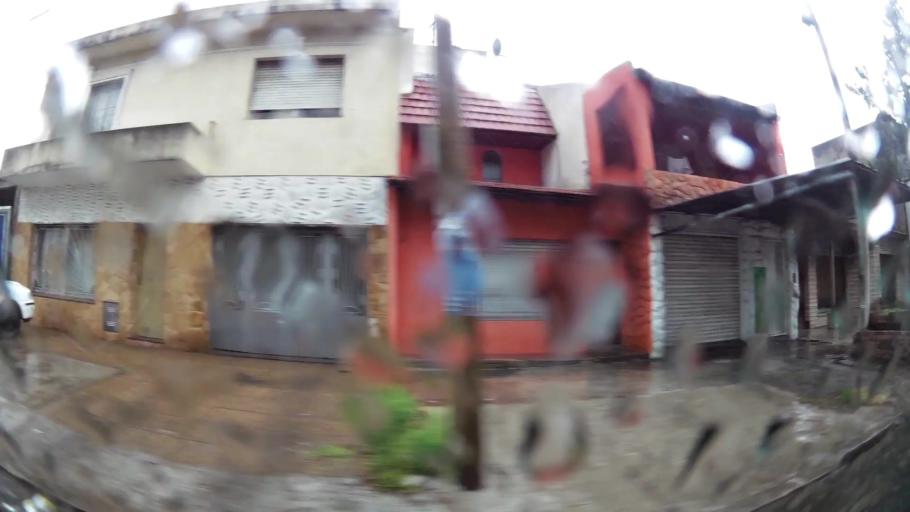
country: AR
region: Buenos Aires
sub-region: Partido de Lanus
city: Lanus
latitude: -34.7128
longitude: -58.4099
